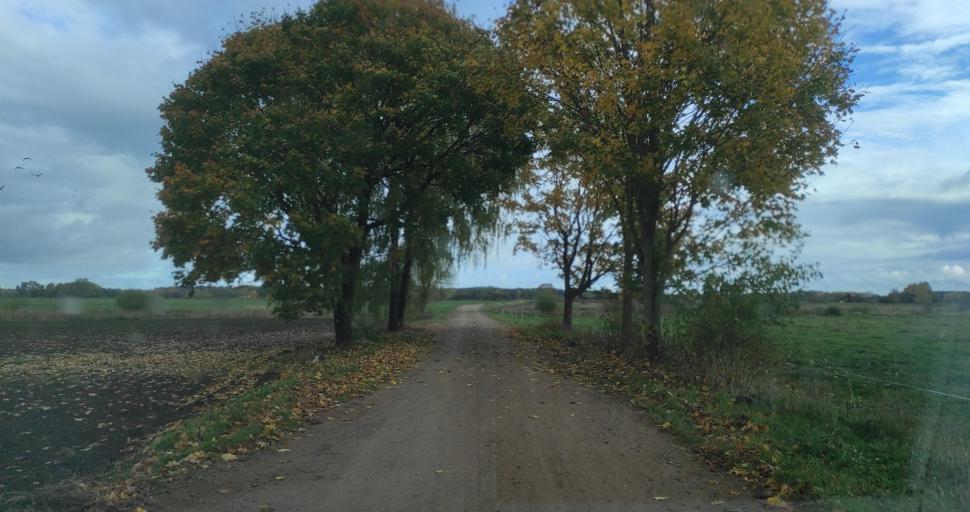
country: LV
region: Skrunda
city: Skrunda
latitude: 56.6985
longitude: 22.0087
